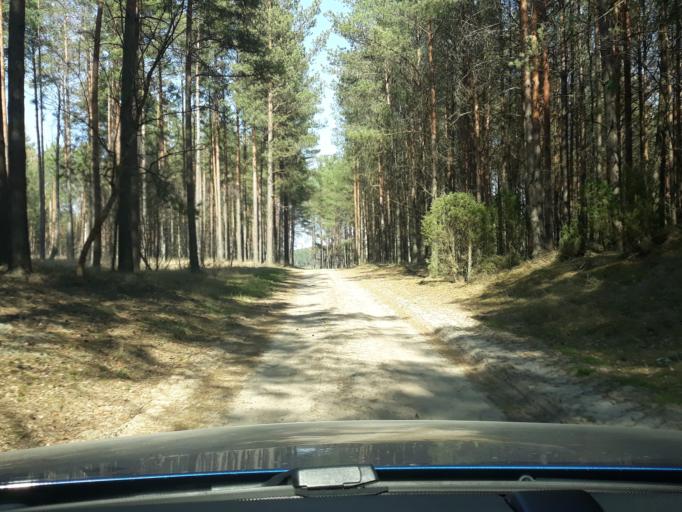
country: PL
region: Pomeranian Voivodeship
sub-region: Powiat bytowski
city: Lipnica
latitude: 53.8689
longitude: 17.4325
